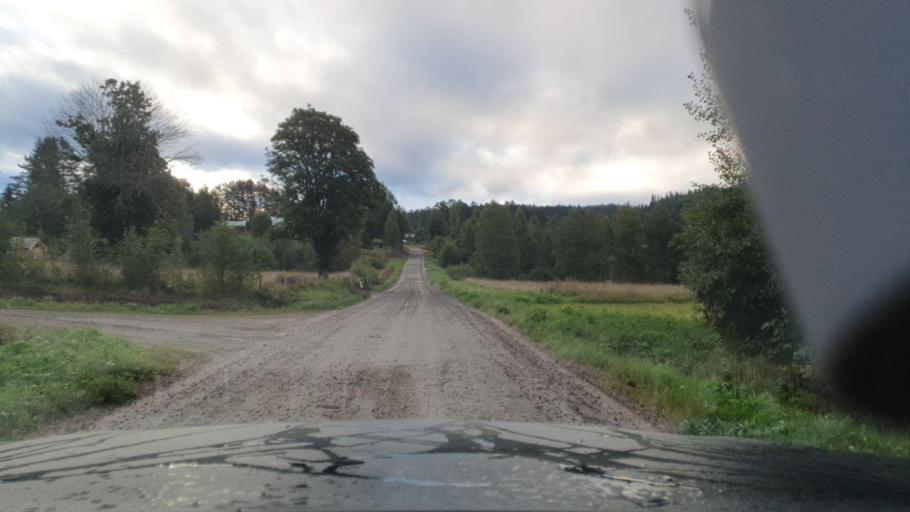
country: SE
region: Vaermland
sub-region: Sunne Kommun
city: Sunne
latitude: 60.0353
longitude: 13.2302
